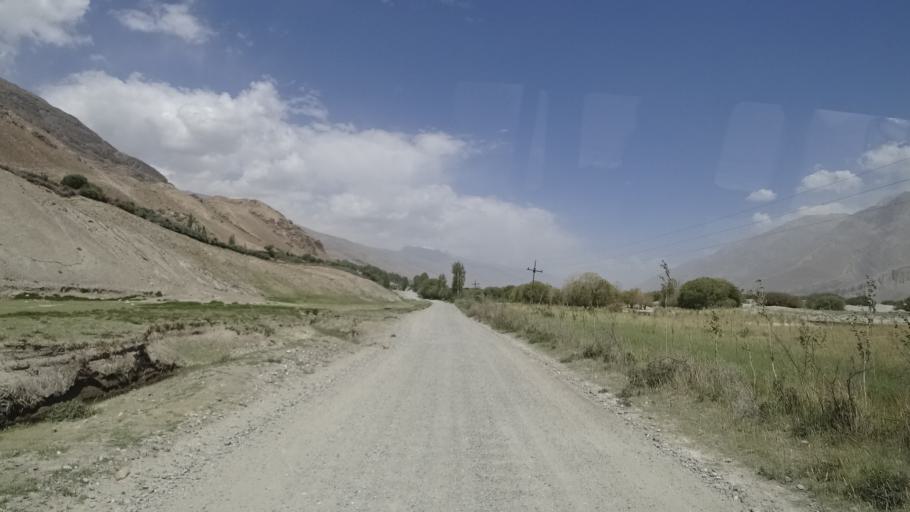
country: AF
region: Badakhshan
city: Khandud
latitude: 36.9328
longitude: 72.2113
